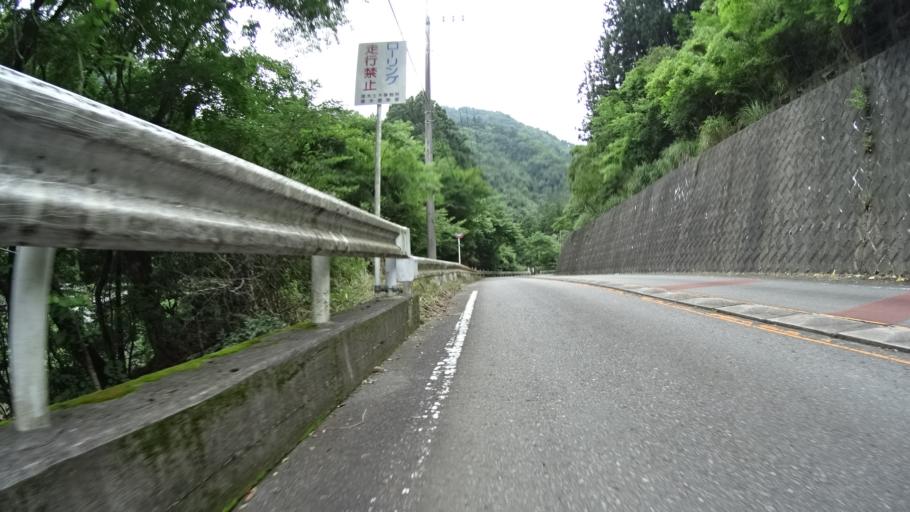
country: JP
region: Kanagawa
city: Hadano
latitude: 35.5000
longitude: 139.2318
